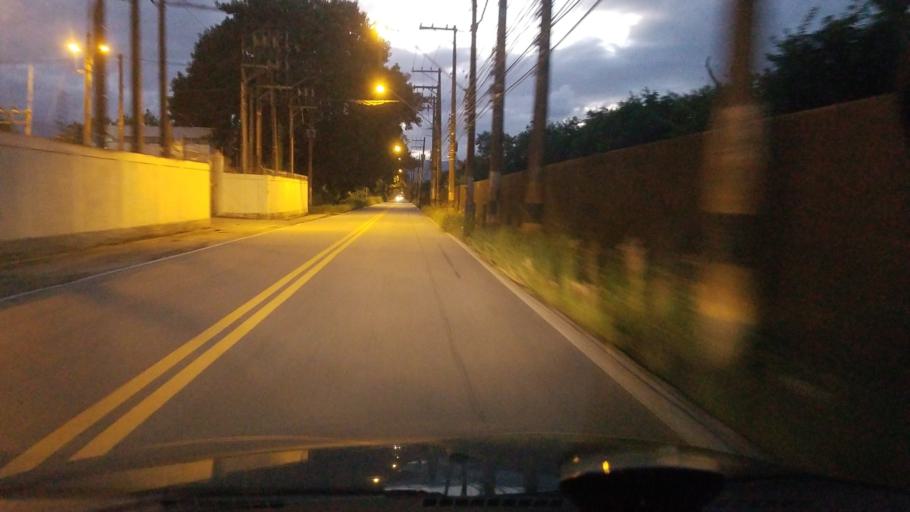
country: BR
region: Sao Paulo
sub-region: Sao Vicente
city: Sao Vicente
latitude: -23.9257
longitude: -46.3827
